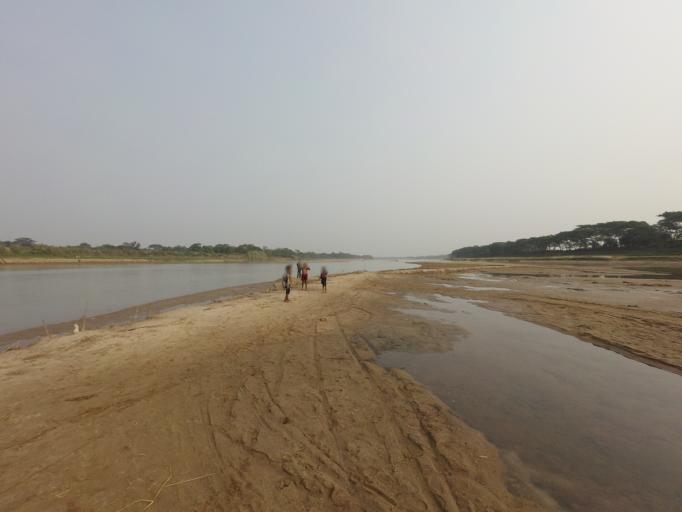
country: BD
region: Dhaka
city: Netrakona
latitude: 25.1026
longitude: 90.6553
